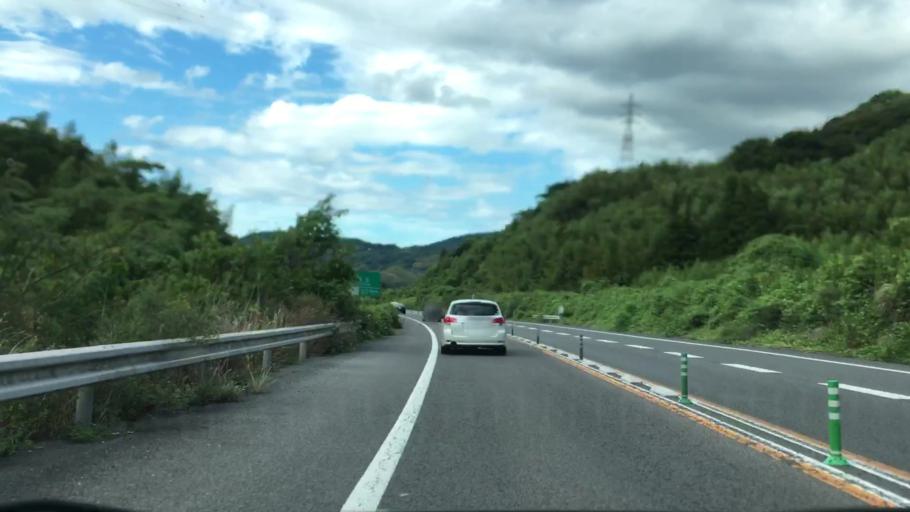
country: JP
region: Saga Prefecture
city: Karatsu
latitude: 33.4323
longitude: 130.0484
